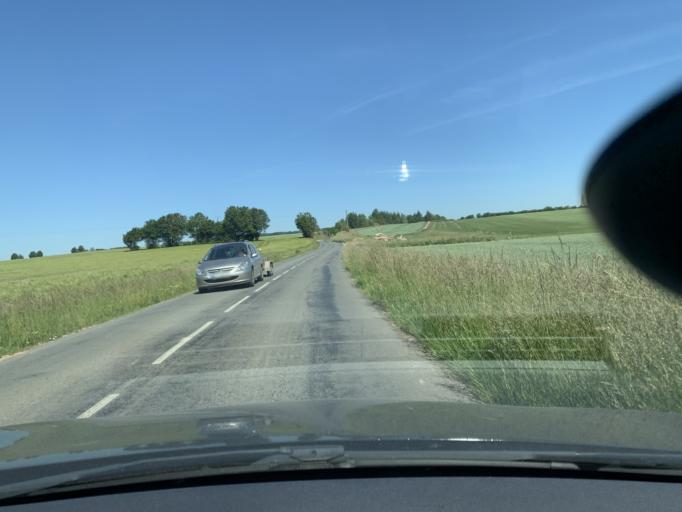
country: FR
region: Nord-Pas-de-Calais
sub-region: Departement du Nord
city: Fontaine-Notre-Dame
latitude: 50.1539
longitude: 3.1649
